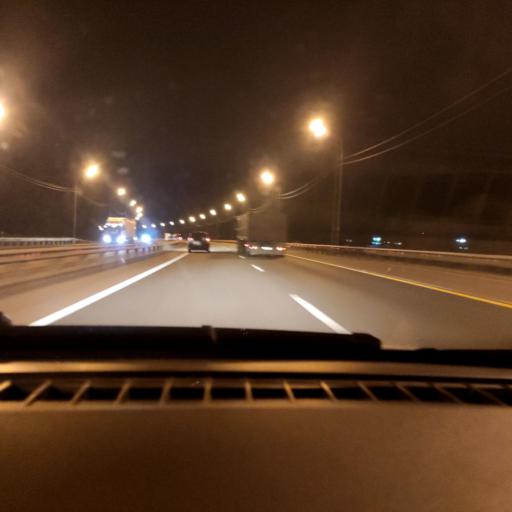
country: RU
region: Lipetsk
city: Khlevnoye
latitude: 52.2485
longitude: 39.0657
